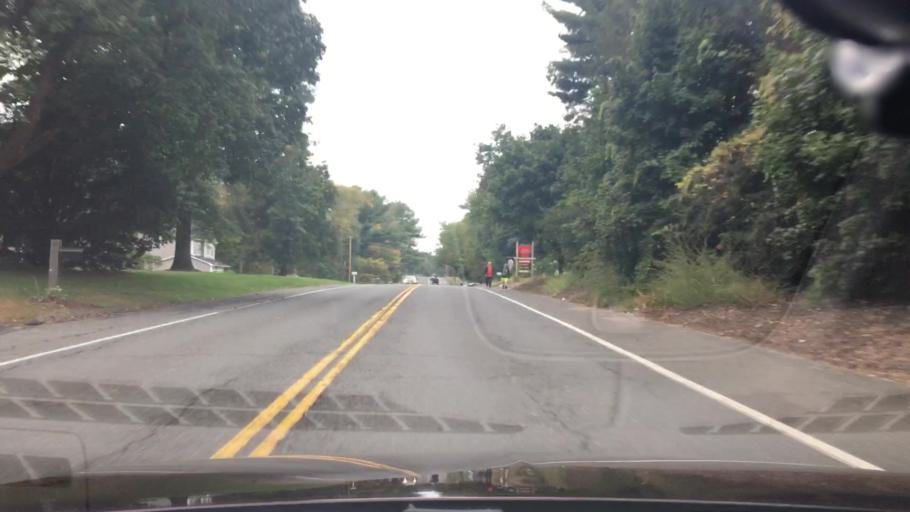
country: US
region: Massachusetts
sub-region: Hampden County
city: East Longmeadow
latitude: 42.0490
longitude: -72.4792
